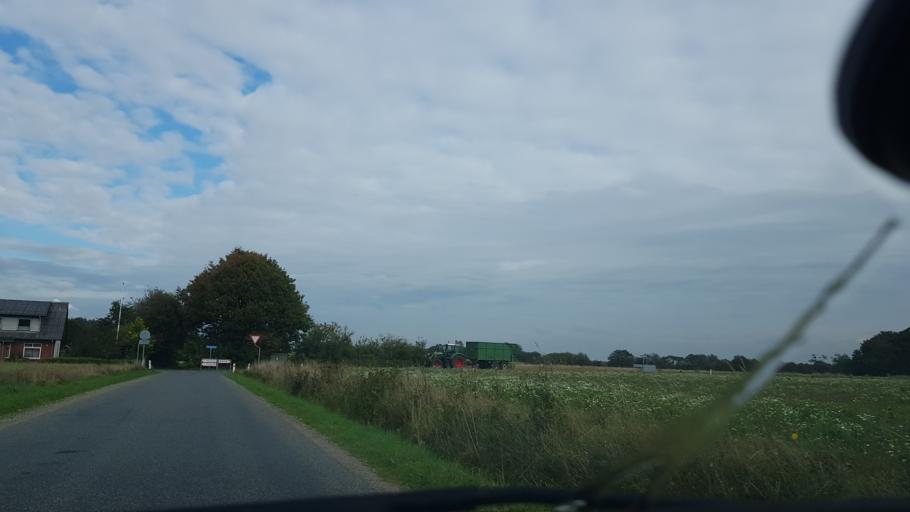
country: DK
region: South Denmark
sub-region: Vejen Kommune
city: Brorup
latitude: 55.4872
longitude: 8.9862
